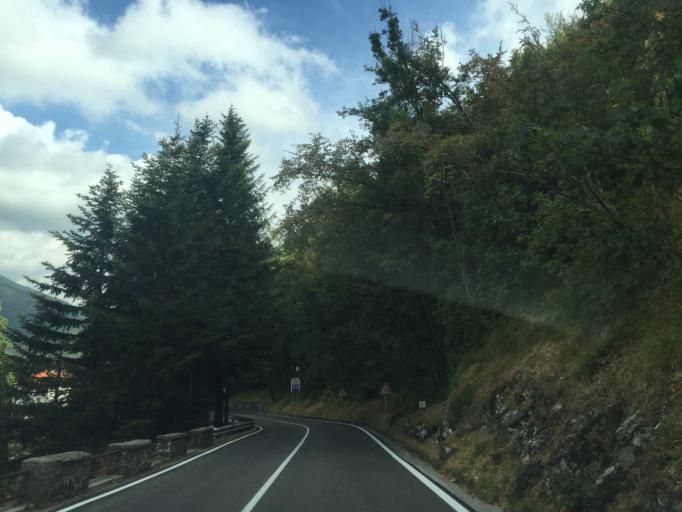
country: IT
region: Tuscany
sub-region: Provincia di Pistoia
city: Cutigliano
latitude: 44.1200
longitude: 10.7263
